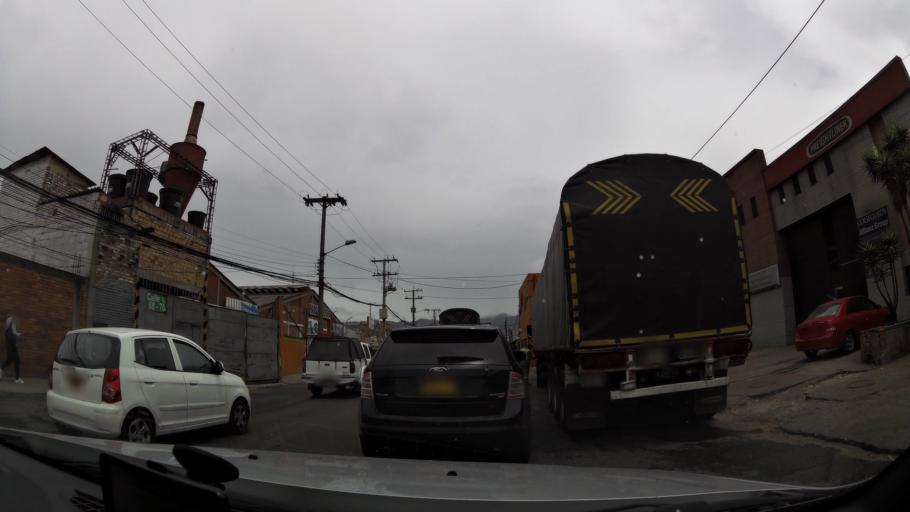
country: CO
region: Bogota D.C.
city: Bogota
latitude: 4.6432
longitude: -74.1138
